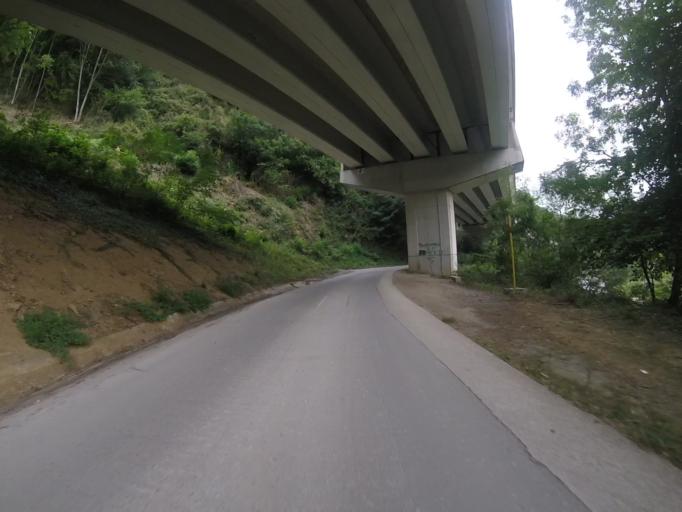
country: ES
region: Navarre
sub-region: Provincia de Navarra
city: Sunbilla
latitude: 43.1793
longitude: -1.6707
